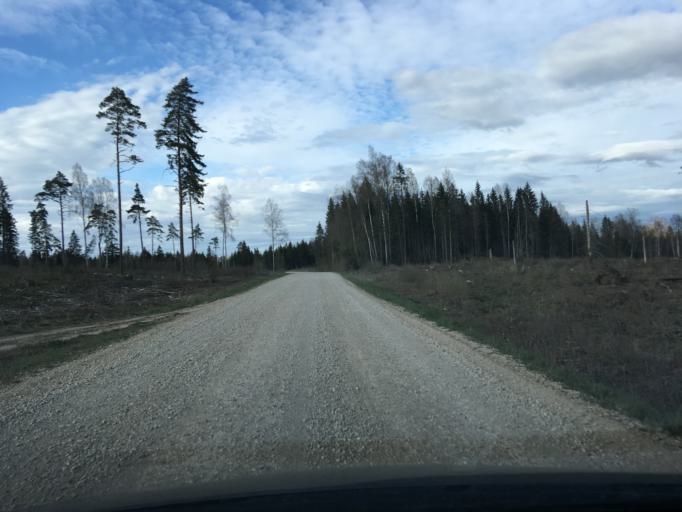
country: EE
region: Raplamaa
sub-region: Maerjamaa vald
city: Marjamaa
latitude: 58.9593
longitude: 24.3278
